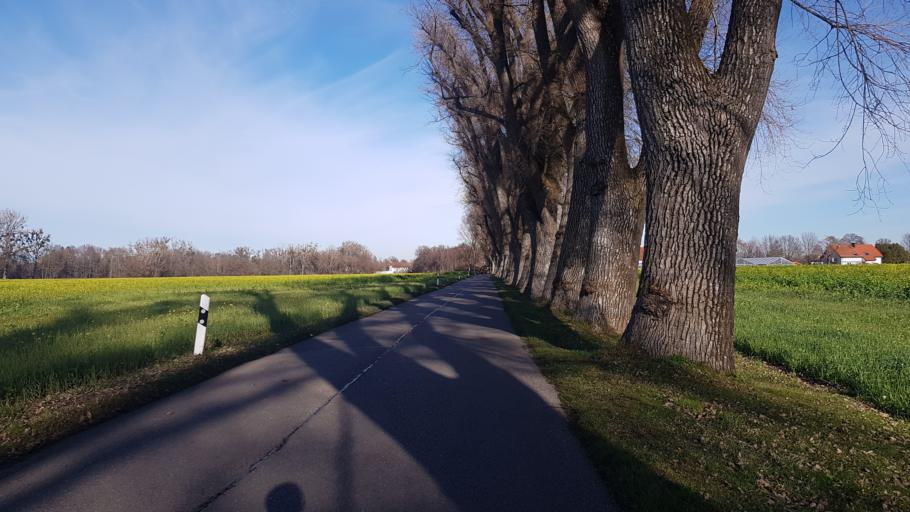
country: DE
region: Bavaria
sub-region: Upper Bavaria
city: Karlsfeld
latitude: 48.2083
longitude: 11.5175
